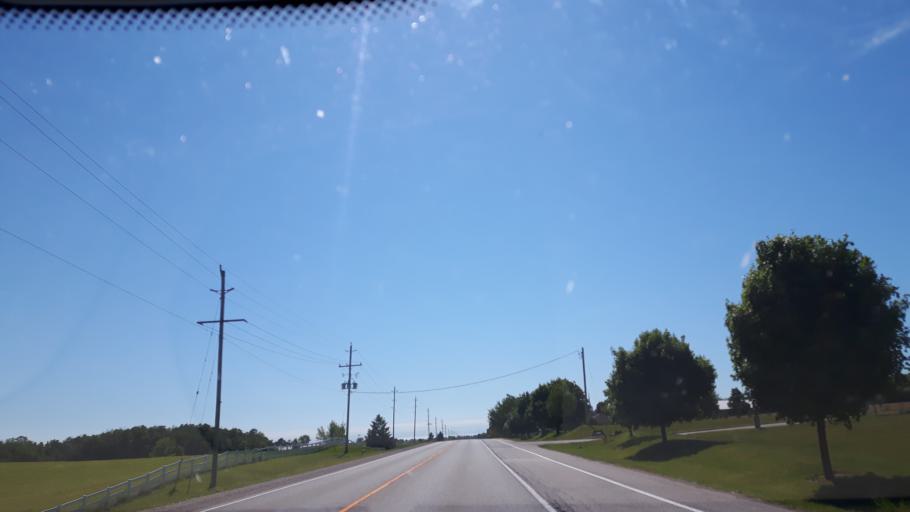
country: CA
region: Ontario
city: Bluewater
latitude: 43.4204
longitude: -81.6320
